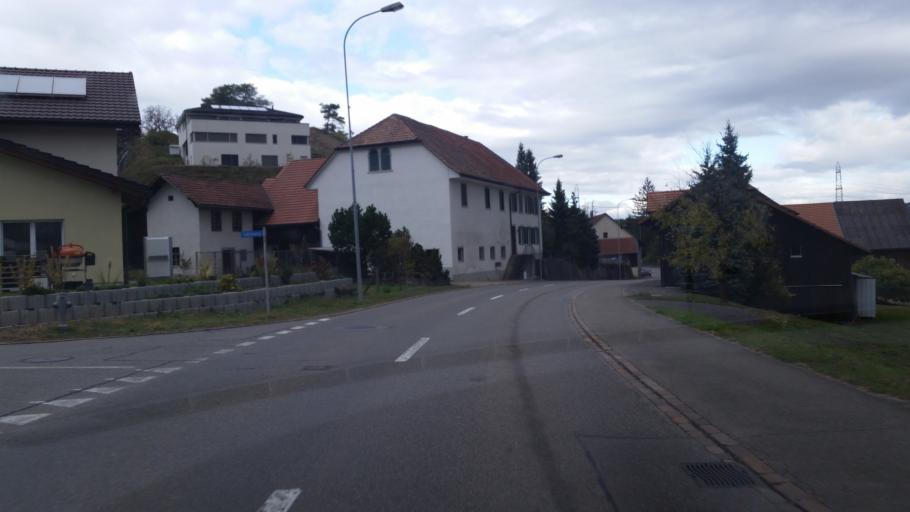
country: CH
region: Aargau
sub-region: Bezirk Brugg
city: Villigen
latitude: 47.5538
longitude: 8.2219
